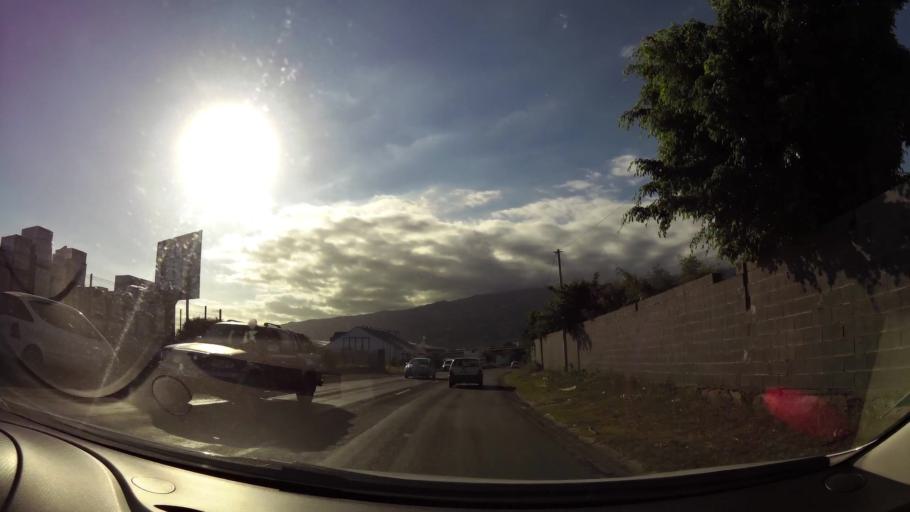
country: RE
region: Reunion
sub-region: Reunion
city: Saint-Louis
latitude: -21.2873
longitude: 55.3979
